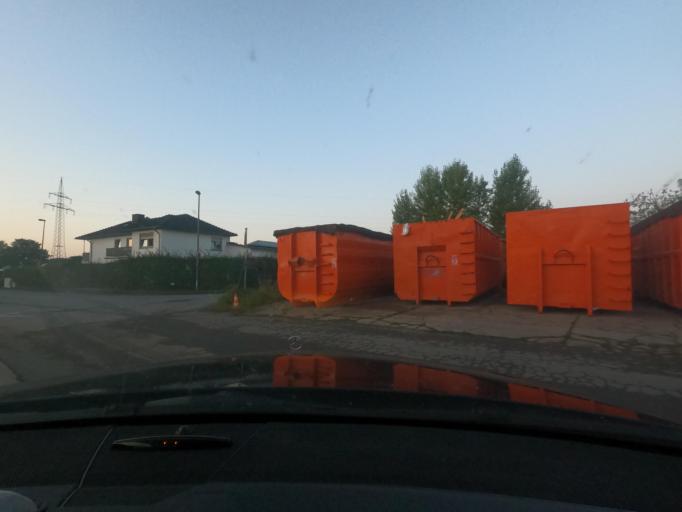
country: DE
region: North Rhine-Westphalia
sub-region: Regierungsbezirk Detmold
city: Salzkotten
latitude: 51.6681
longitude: 8.5916
